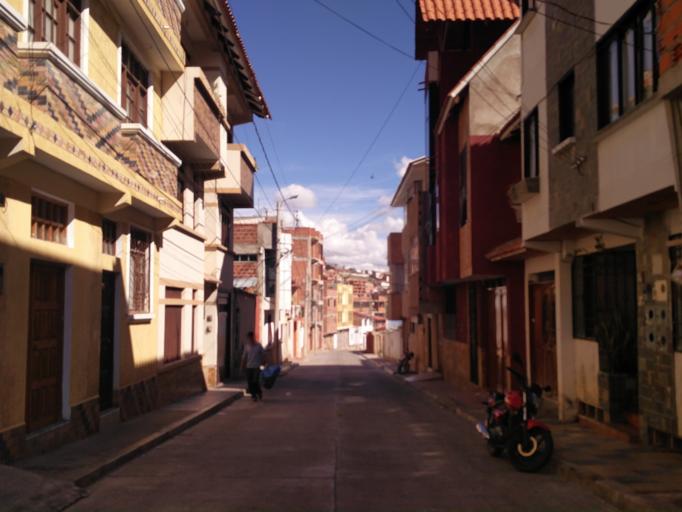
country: BO
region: Chuquisaca
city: Sucre
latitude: -19.0374
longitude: -65.2472
